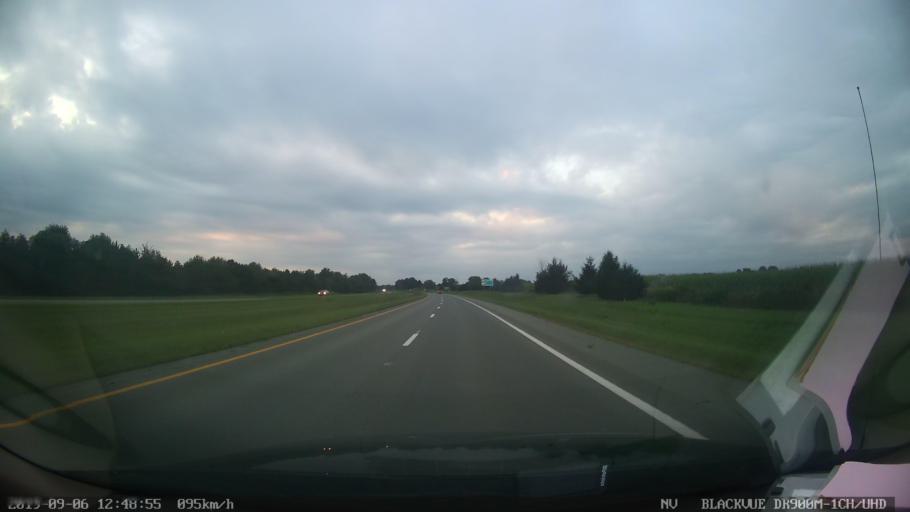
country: US
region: Ohio
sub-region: Knox County
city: Fredericktown
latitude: 40.4619
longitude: -82.5479
